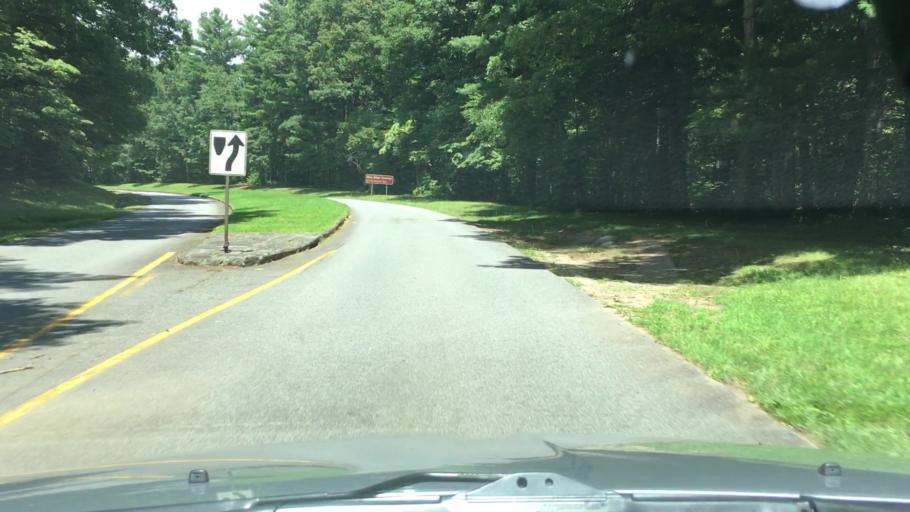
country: US
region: North Carolina
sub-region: Buncombe County
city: Asheville
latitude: 35.5921
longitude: -82.4788
